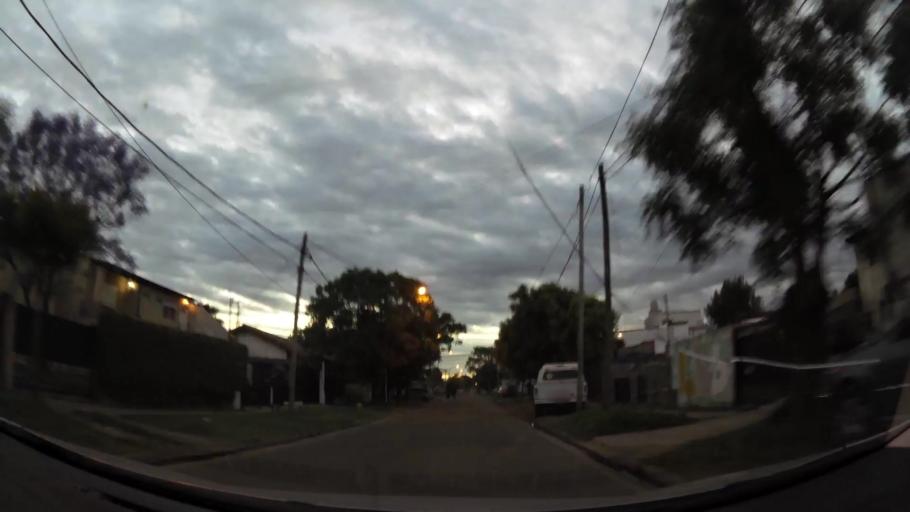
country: AR
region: Buenos Aires
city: Santa Catalina - Dique Lujan
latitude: -34.4152
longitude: -58.6886
